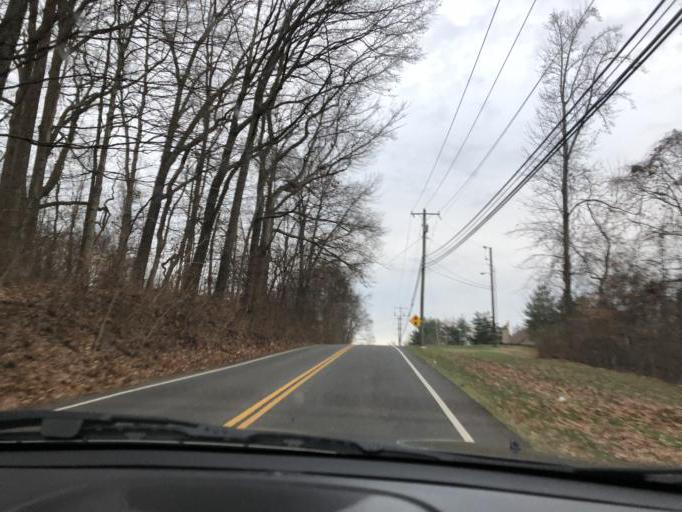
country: US
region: Tennessee
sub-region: Wilson County
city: Green Hill
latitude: 36.1907
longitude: -86.5930
